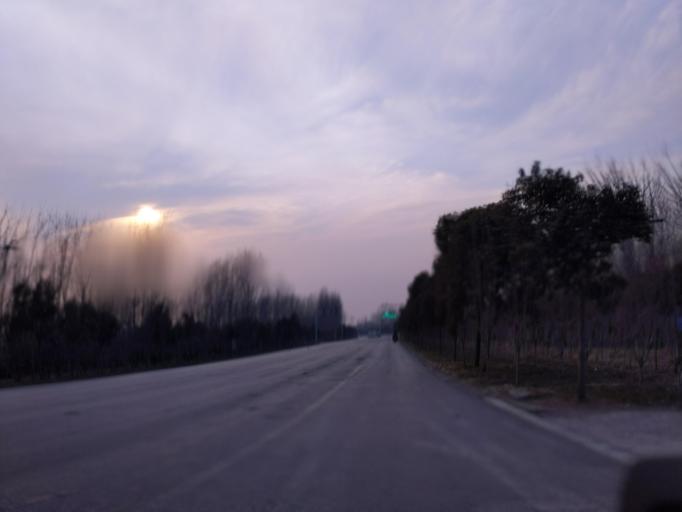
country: CN
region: Henan Sheng
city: Puyang
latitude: 35.8200
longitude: 114.9831
